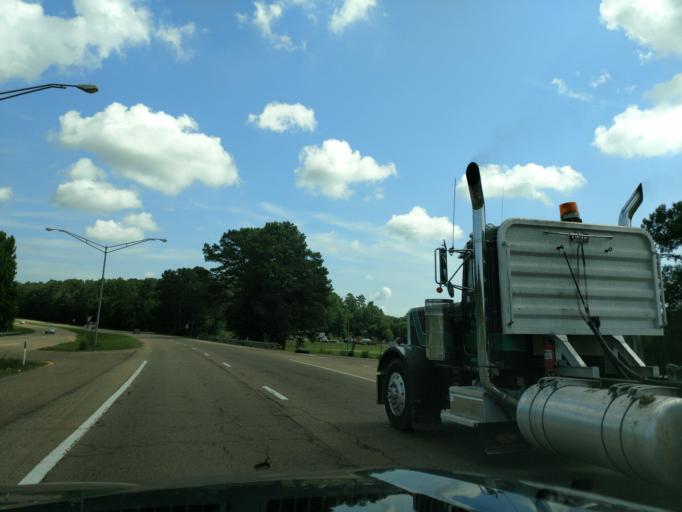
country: US
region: Mississippi
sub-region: Simpson County
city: Magee
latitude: 31.8885
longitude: -89.7631
